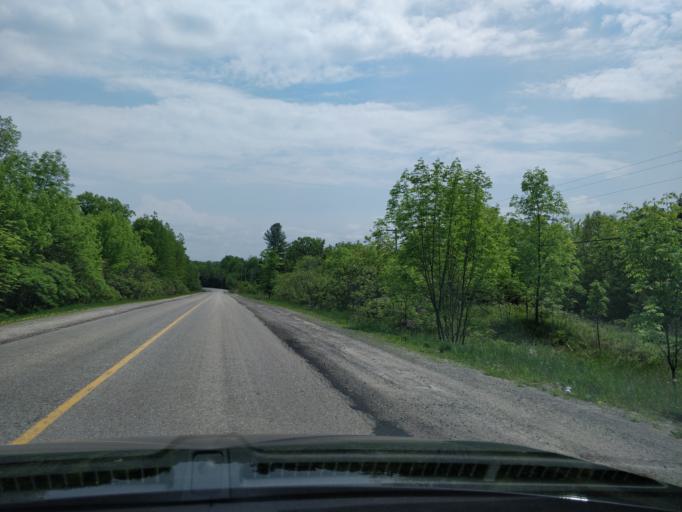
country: CA
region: Ontario
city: Perth
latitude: 44.6402
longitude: -76.5296
